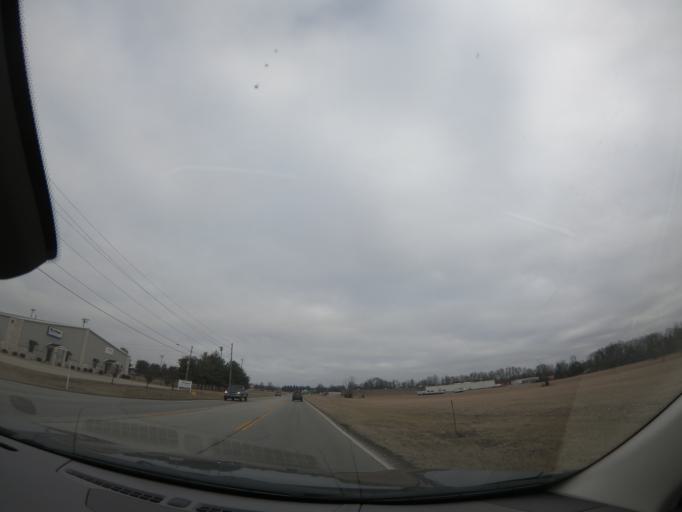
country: US
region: Kentucky
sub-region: Nelson County
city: Bardstown
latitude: 37.8271
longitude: -85.4286
